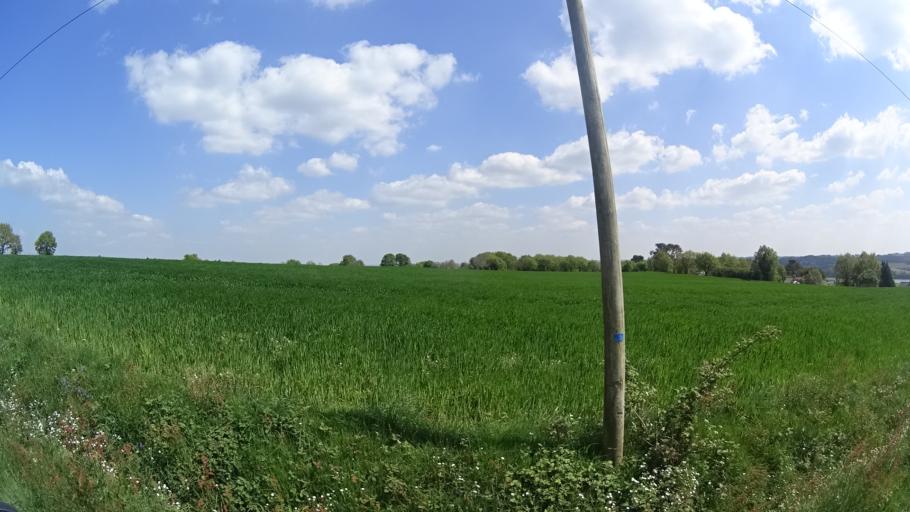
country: FR
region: Brittany
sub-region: Departement du Morbihan
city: Beganne
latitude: 47.5869
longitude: -2.2545
